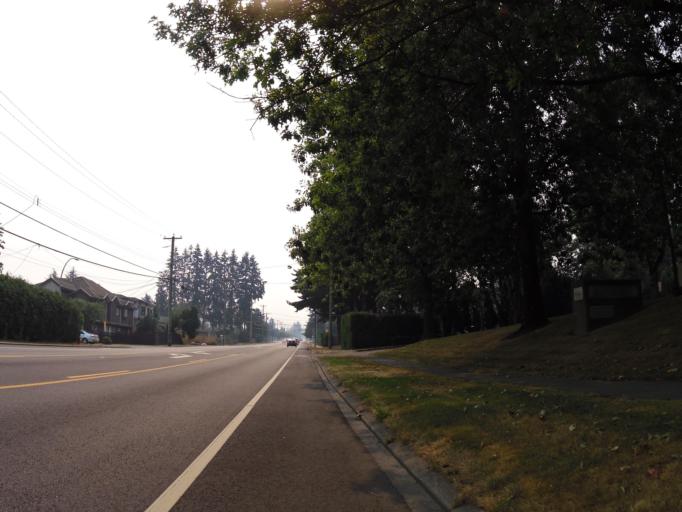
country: CA
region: British Columbia
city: Surrey
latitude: 49.1215
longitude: -122.8566
